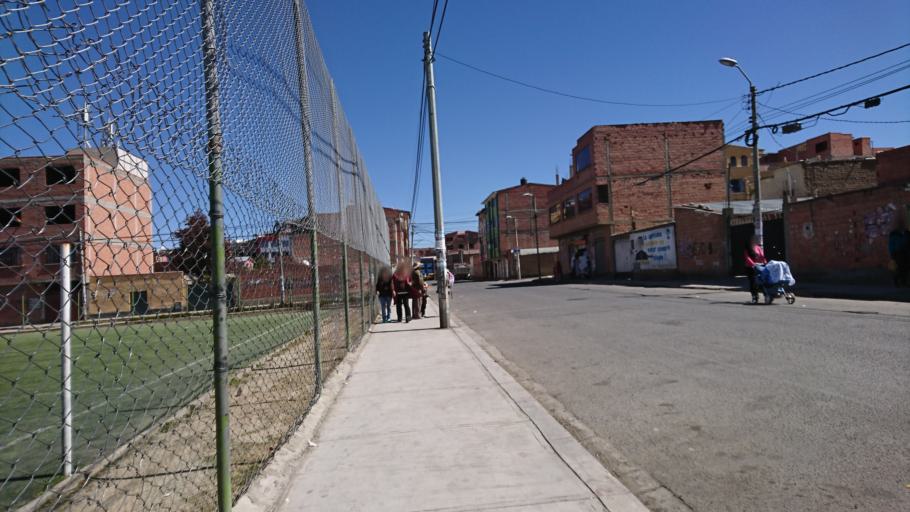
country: BO
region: La Paz
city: La Paz
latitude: -16.5008
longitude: -68.1025
